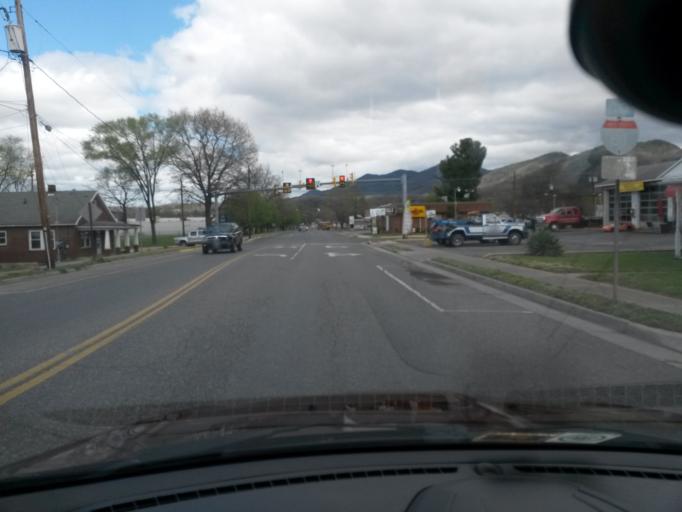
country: US
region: Virginia
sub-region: City of Buena Vista
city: Buena Vista
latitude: 37.7225
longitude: -79.3632
